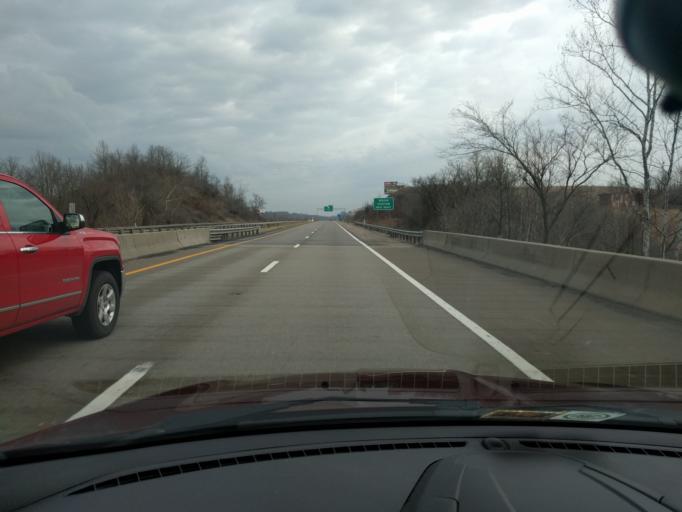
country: US
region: West Virginia
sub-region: Wood County
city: Mineral Wells
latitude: 39.1667
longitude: -81.5401
